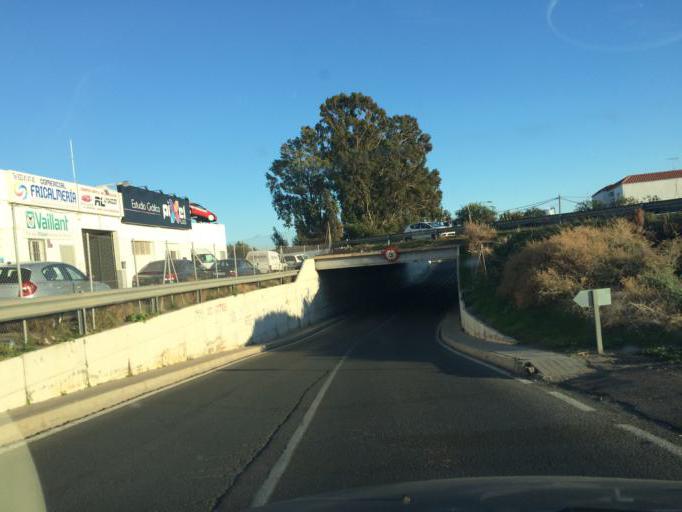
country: ES
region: Andalusia
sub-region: Provincia de Almeria
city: Almeria
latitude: 36.8428
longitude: -2.4274
